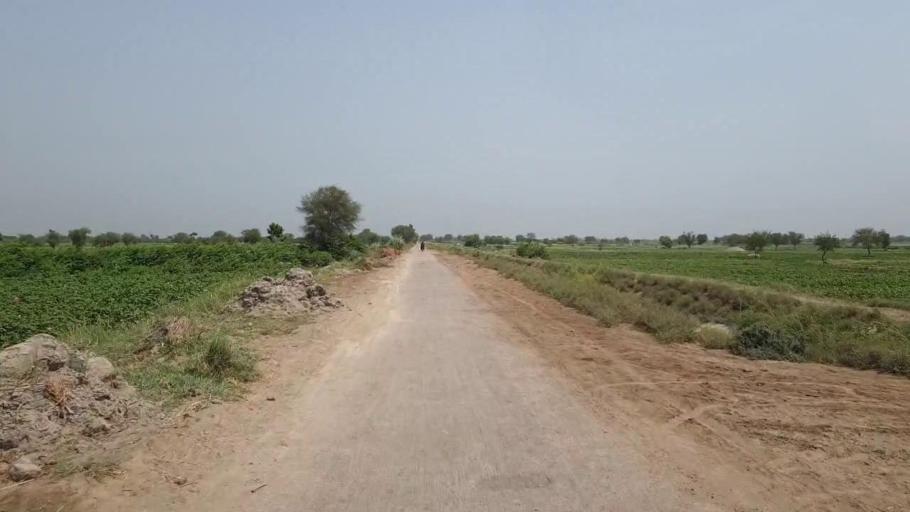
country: PK
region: Sindh
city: Nawabshah
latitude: 26.2729
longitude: 68.3147
